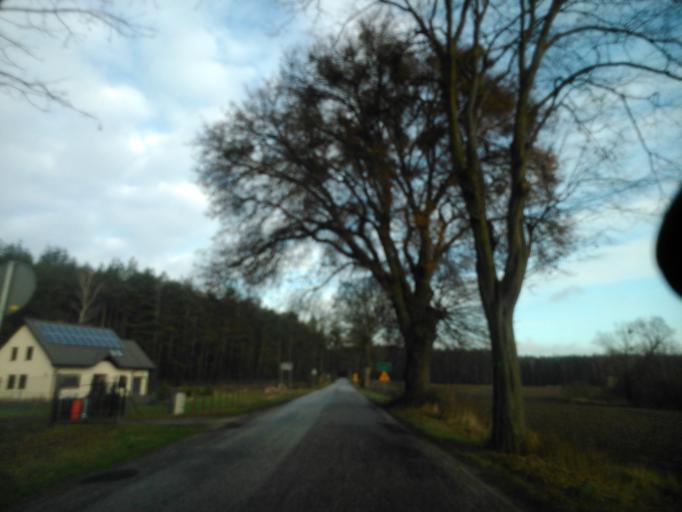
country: PL
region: Kujawsko-Pomorskie
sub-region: Powiat golubsko-dobrzynski
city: Golub-Dobrzyn
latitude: 53.1365
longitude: 19.1018
